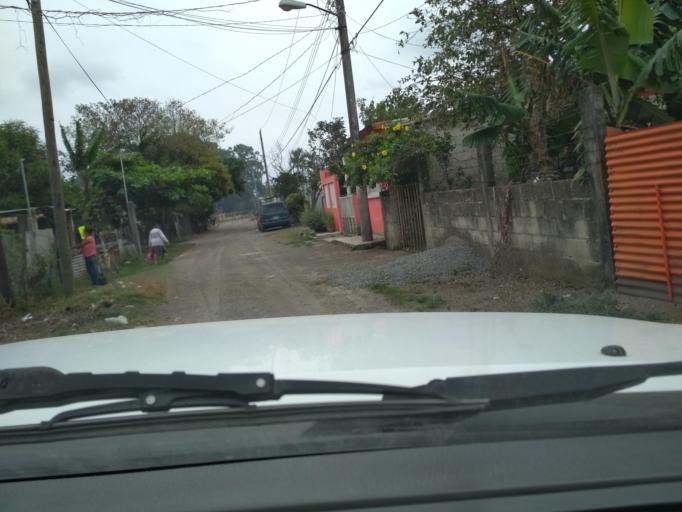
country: MX
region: Veracruz
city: Paso del Toro
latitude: 19.0536
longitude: -96.1356
